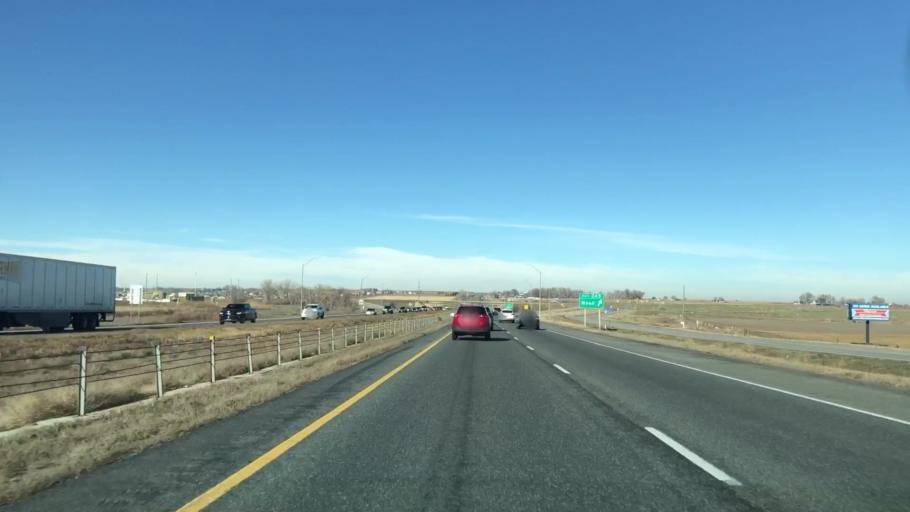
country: US
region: Colorado
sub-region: Weld County
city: Mead
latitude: 40.2282
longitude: -104.9800
